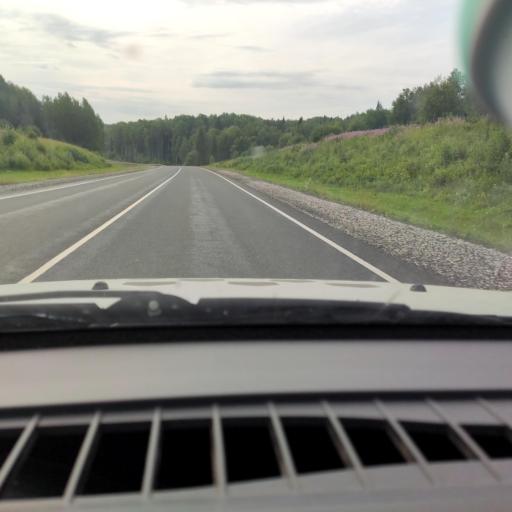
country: RU
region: Kirov
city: Kostino
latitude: 58.6561
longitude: 53.7722
